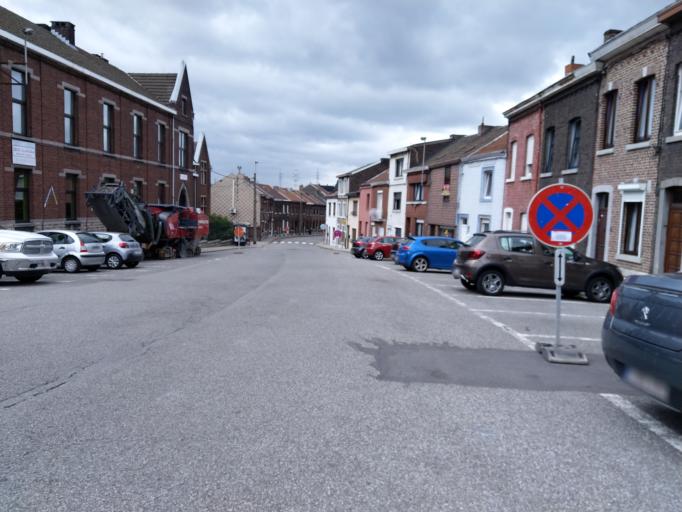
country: BE
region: Wallonia
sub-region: Province de Liege
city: Saint-Nicolas
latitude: 50.6207
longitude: 5.5320
